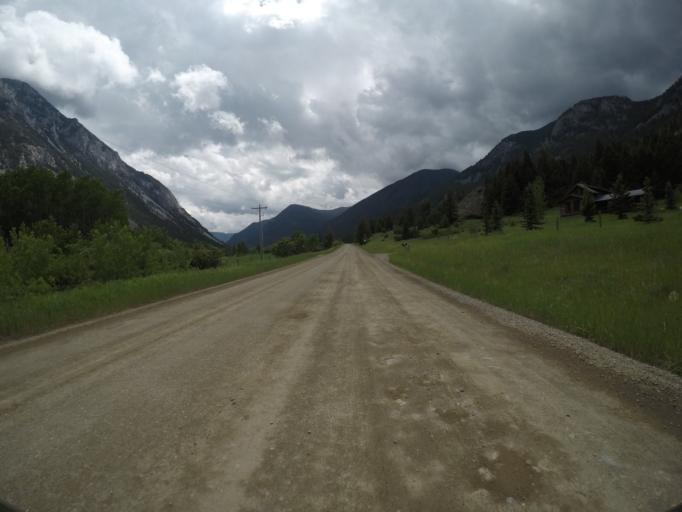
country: US
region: Montana
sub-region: Park County
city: Livingston
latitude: 45.5160
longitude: -110.2264
